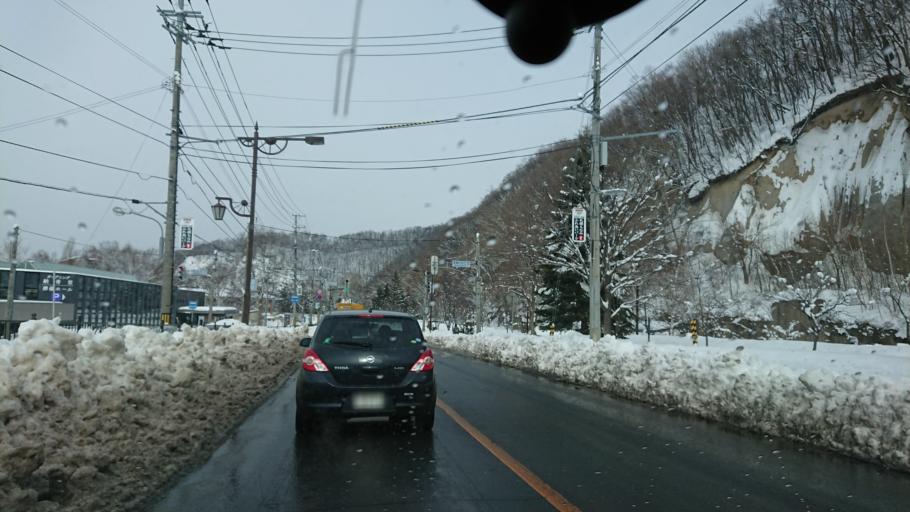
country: JP
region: Hokkaido
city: Sapporo
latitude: 42.9796
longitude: 141.3437
